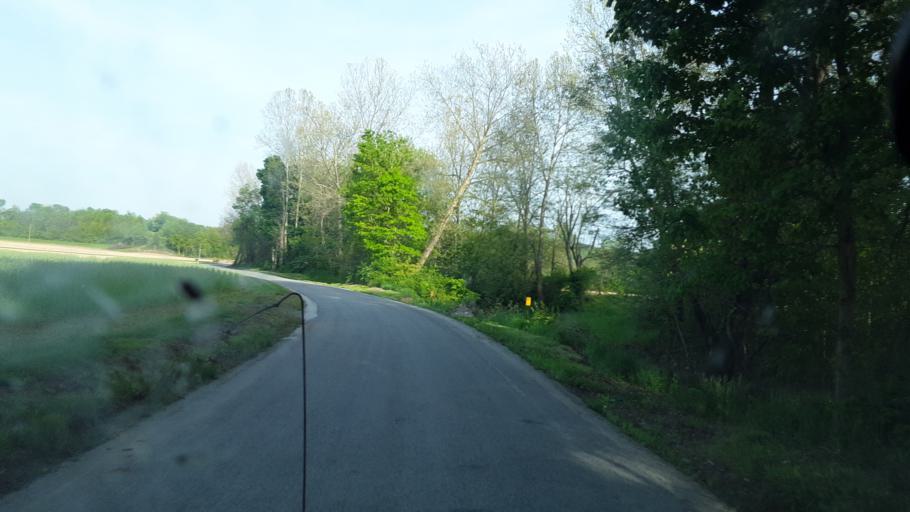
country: US
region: Ohio
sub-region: Ross County
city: Kingston
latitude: 39.4997
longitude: -82.7283
